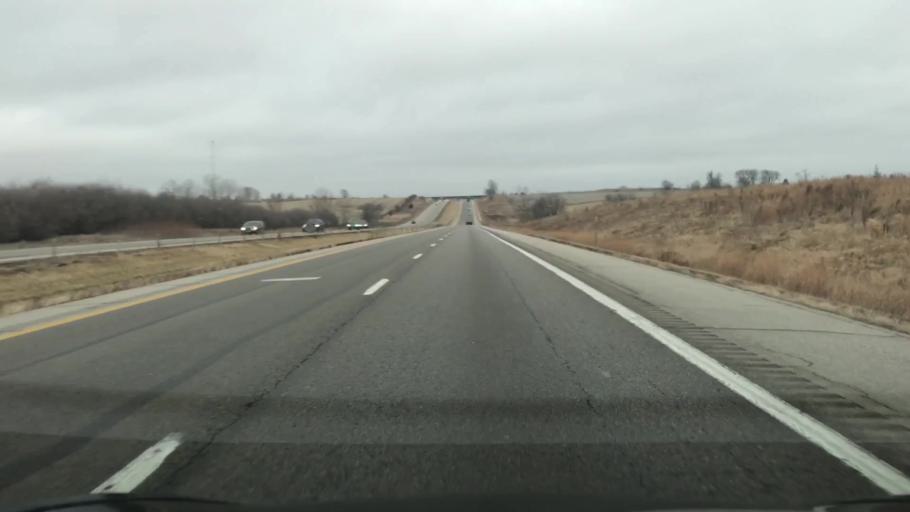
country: US
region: Iowa
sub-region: Madison County
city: Earlham
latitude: 41.5001
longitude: -94.2132
